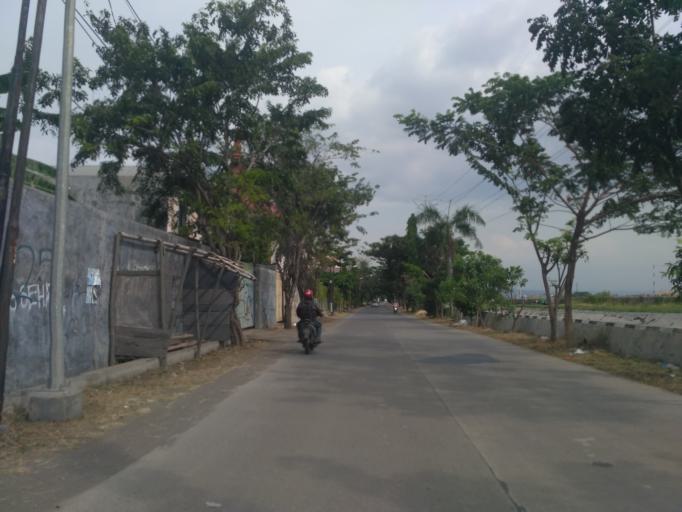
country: ID
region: Central Java
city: Semarang
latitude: -6.9629
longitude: 110.4015
